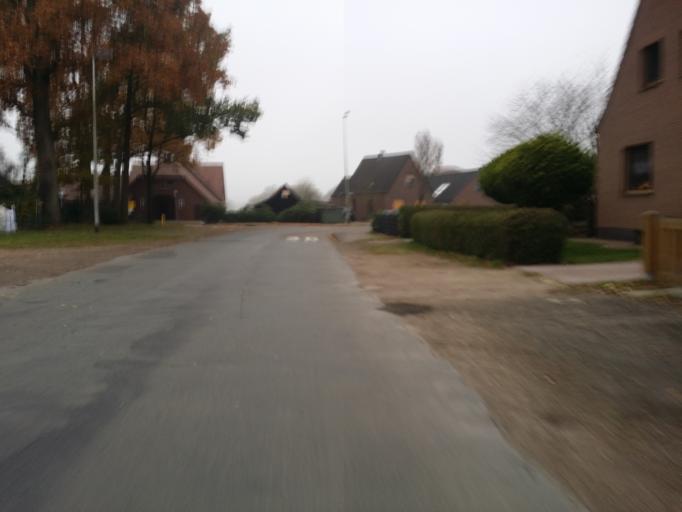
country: DE
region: Lower Saxony
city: Delmenhorst
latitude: 53.0208
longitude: 8.6287
